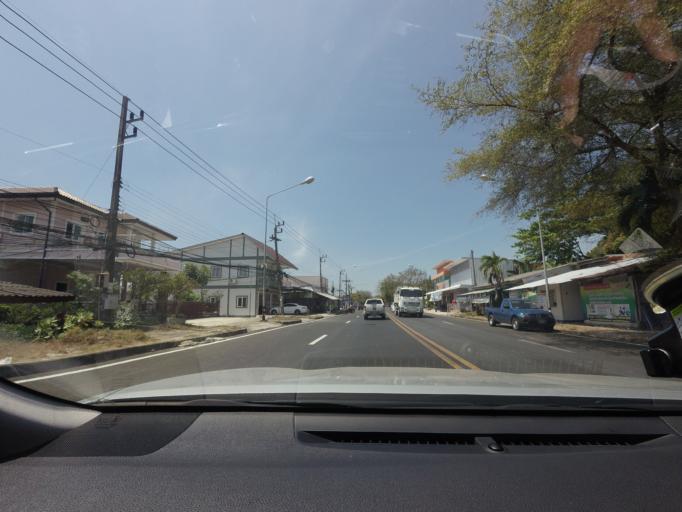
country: TH
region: Narathiwat
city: Narathiwat
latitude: 6.4453
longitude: 101.8128
